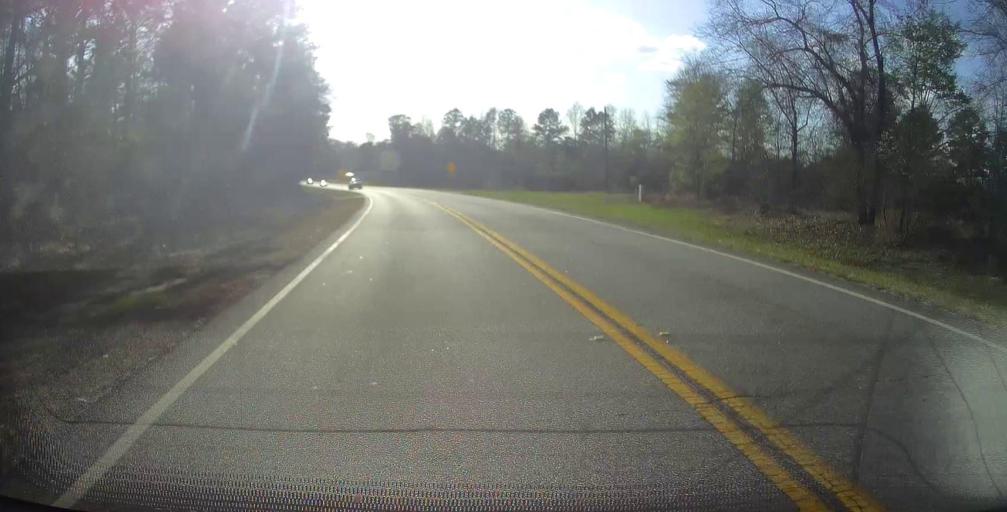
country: US
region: Georgia
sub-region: Montgomery County
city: Mount Vernon
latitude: 32.1904
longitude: -82.6417
